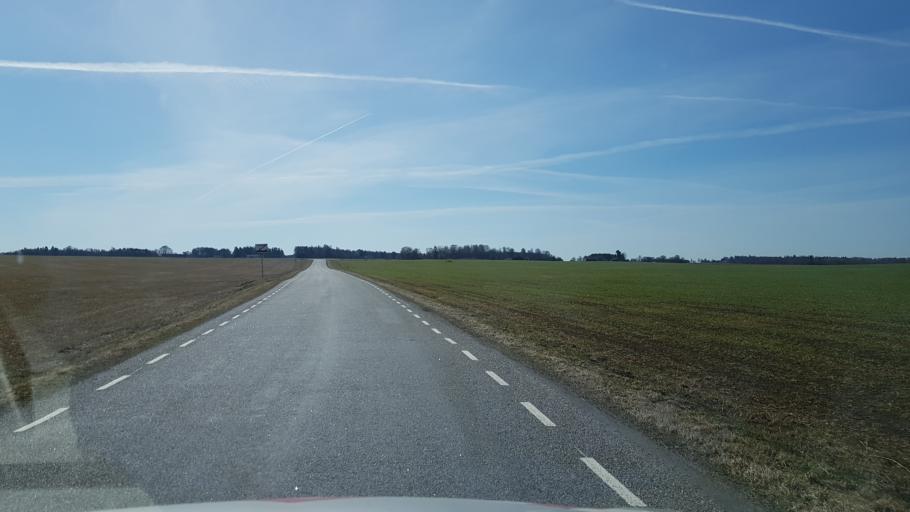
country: EE
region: Laeaene-Virumaa
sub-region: Vinni vald
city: Vinni
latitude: 59.2884
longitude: 26.3847
